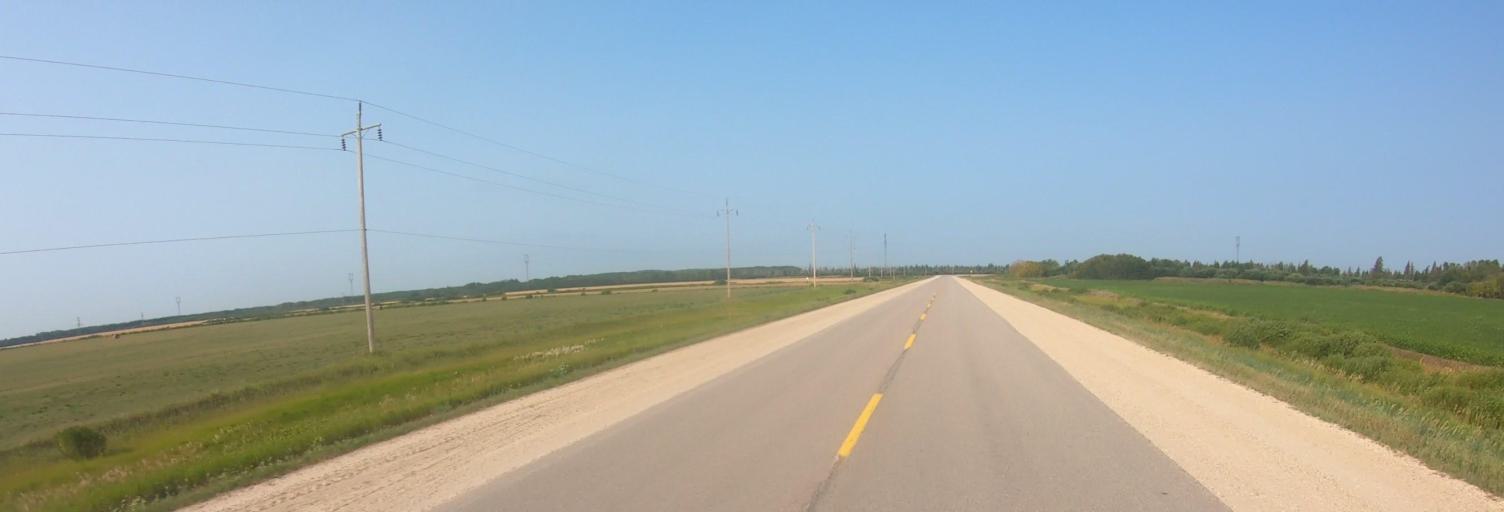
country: US
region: Minnesota
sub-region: Roseau County
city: Warroad
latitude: 49.0159
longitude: -95.5276
